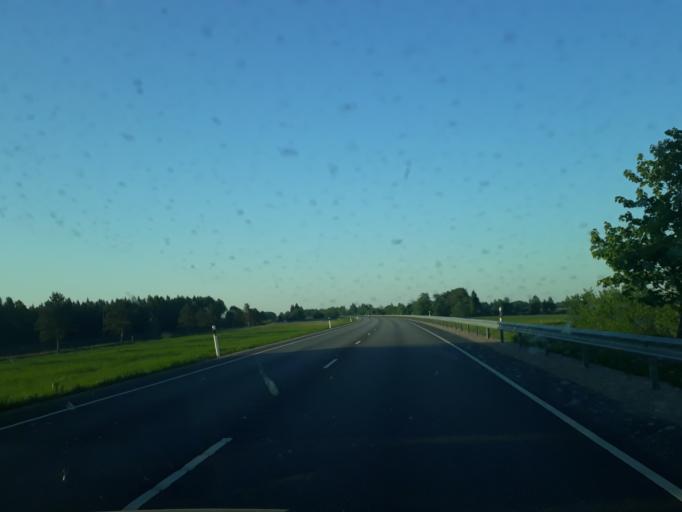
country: EE
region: Paernumaa
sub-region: Tootsi vald
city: Tootsi
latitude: 58.5782
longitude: 24.8880
